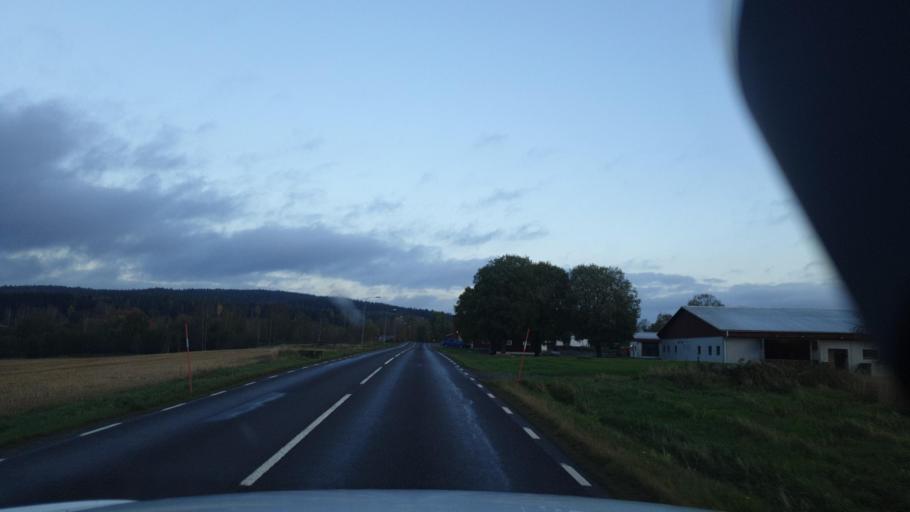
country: SE
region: Vaermland
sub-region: Arvika Kommun
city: Arvika
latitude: 59.7558
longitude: 12.5469
